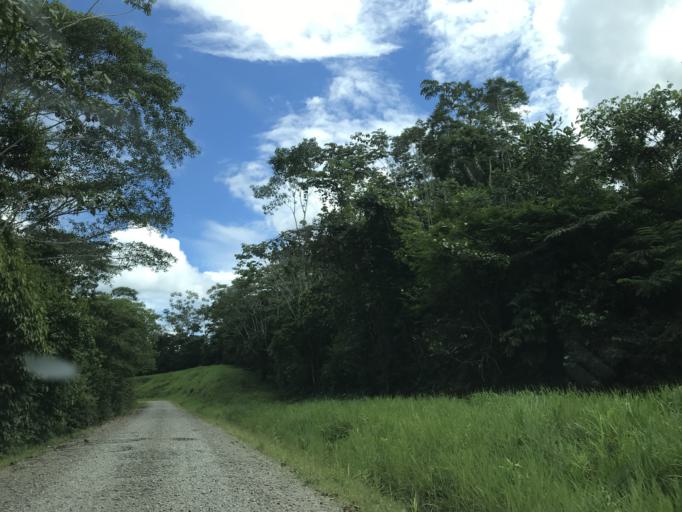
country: EC
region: Orellana
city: Puerto Francisco de Orellana
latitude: -0.6139
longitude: -76.4656
